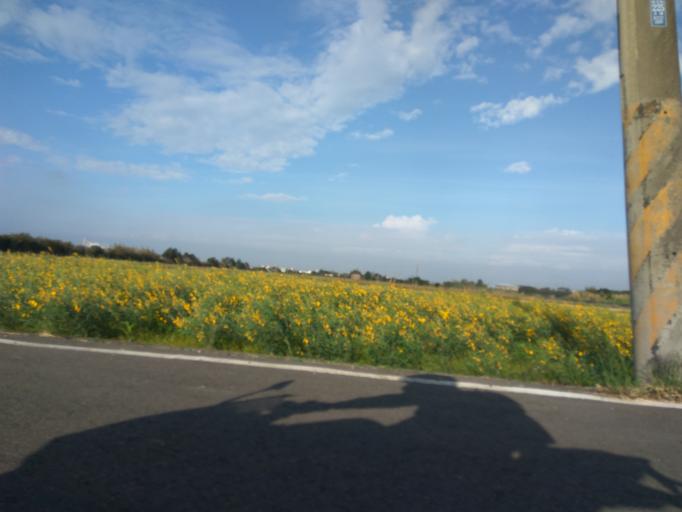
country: TW
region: Taiwan
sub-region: Hsinchu
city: Zhubei
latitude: 24.9793
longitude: 121.0639
